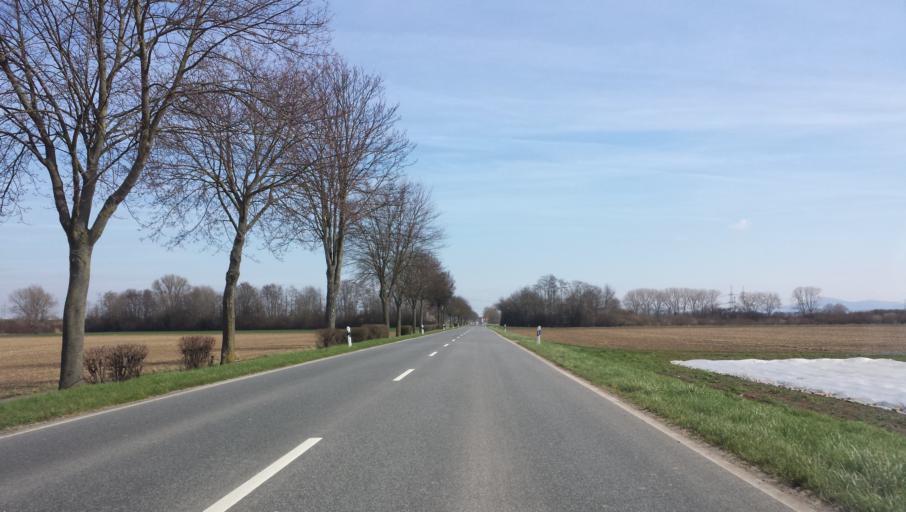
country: DE
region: Rheinland-Pfalz
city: Worms
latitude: 49.6452
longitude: 8.3896
